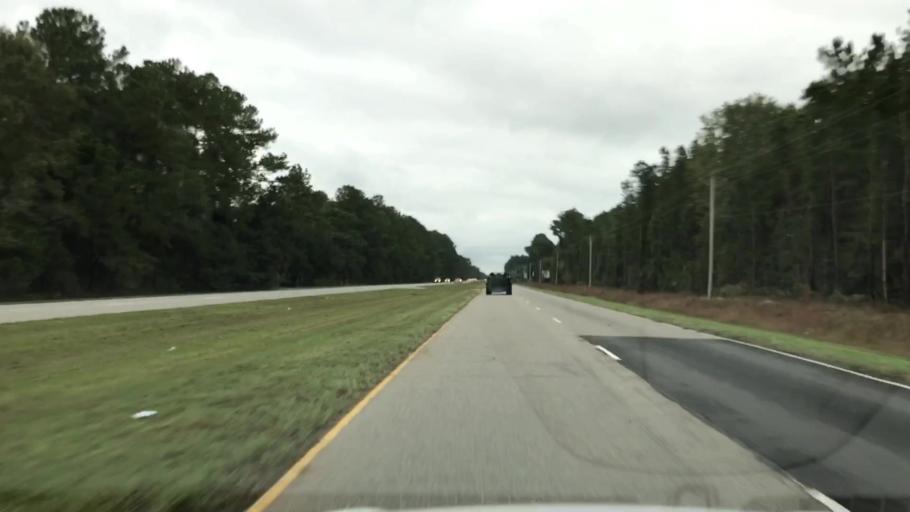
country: US
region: South Carolina
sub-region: Georgetown County
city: Georgetown
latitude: 33.3049
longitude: -79.3369
